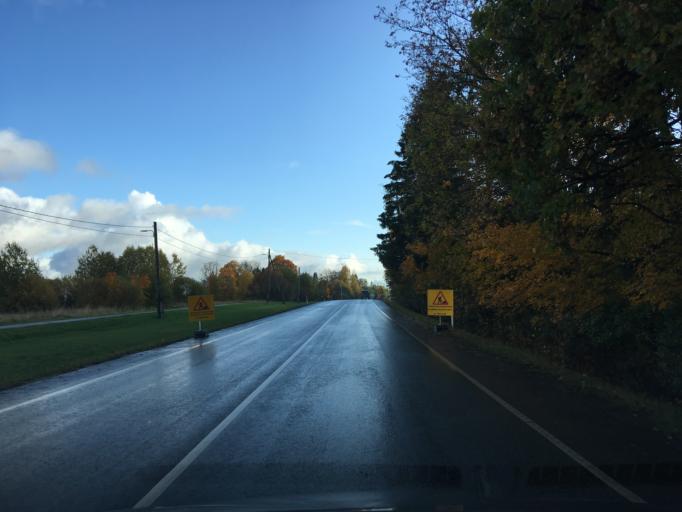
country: EE
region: Harju
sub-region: Saku vald
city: Saku
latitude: 59.2884
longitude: 24.6615
